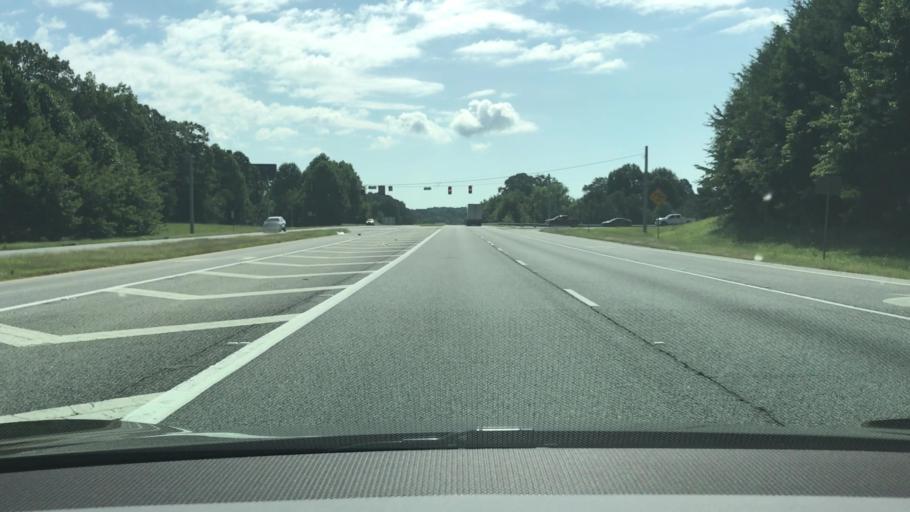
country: US
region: Georgia
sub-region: Habersham County
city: Mount Airy
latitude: 34.5645
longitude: -83.4968
